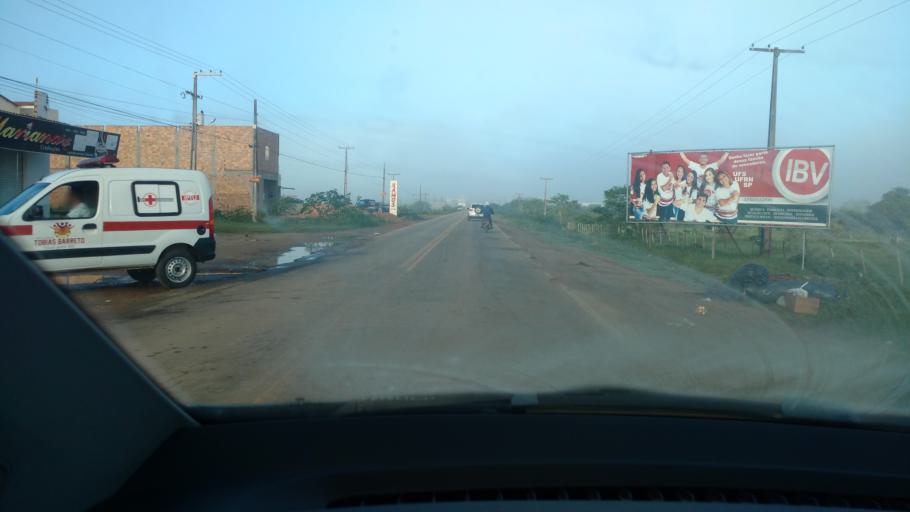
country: BR
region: Sergipe
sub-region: Tobias Barreto
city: Tobias Barreto
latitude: -11.1741
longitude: -37.9891
